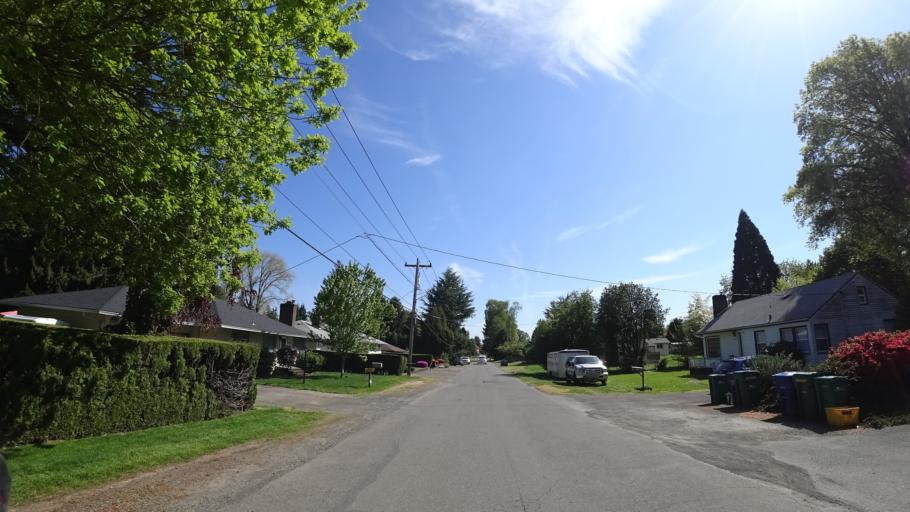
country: US
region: Oregon
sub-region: Clackamas County
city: Milwaukie
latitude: 45.4503
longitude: -122.6248
